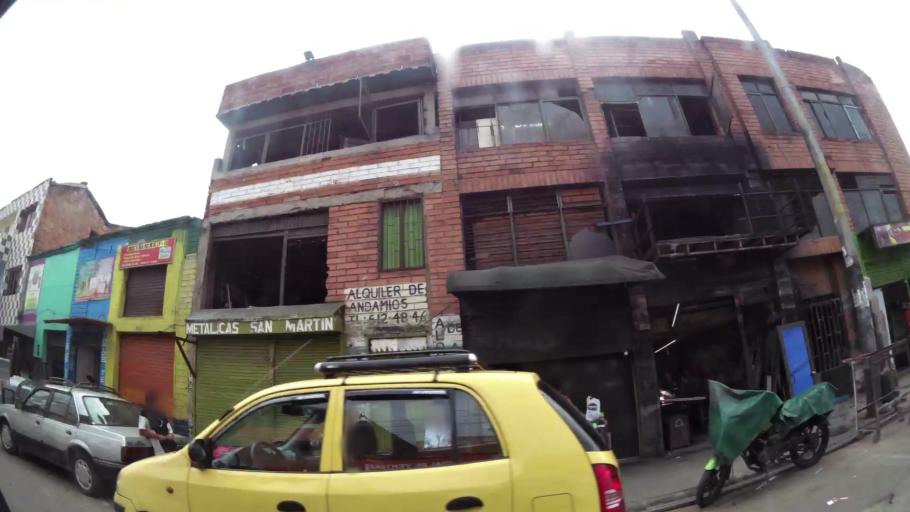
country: CO
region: Antioquia
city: Medellin
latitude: 6.2558
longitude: -75.5691
